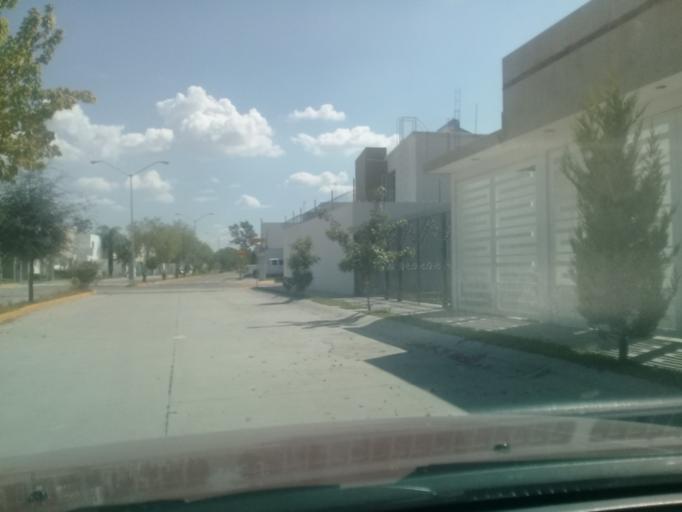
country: MX
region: Aguascalientes
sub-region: Aguascalientes
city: La Loma de los Negritos
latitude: 21.8420
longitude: -102.3271
